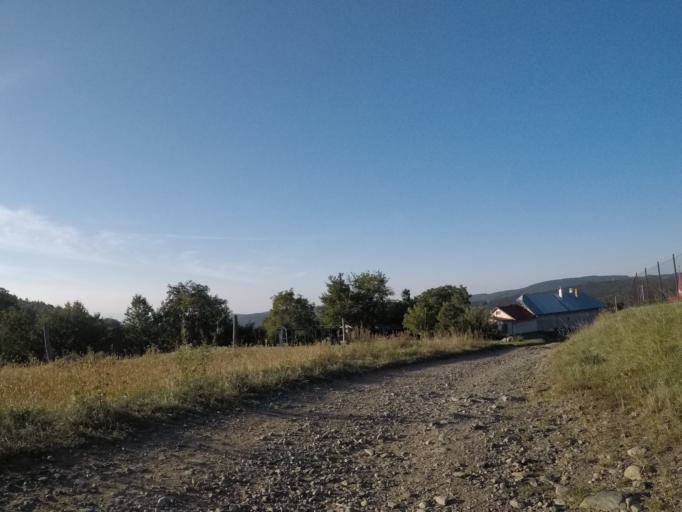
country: SK
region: Kosicky
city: Kosice
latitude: 48.7470
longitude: 21.1260
